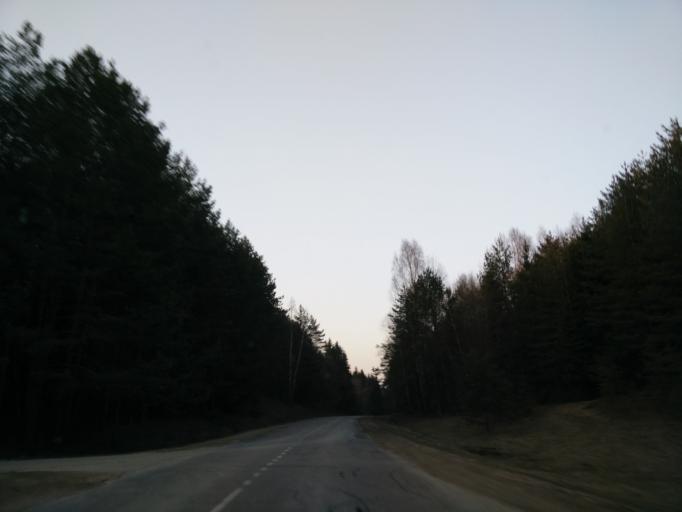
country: LT
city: Trakai
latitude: 54.7038
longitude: 24.9654
